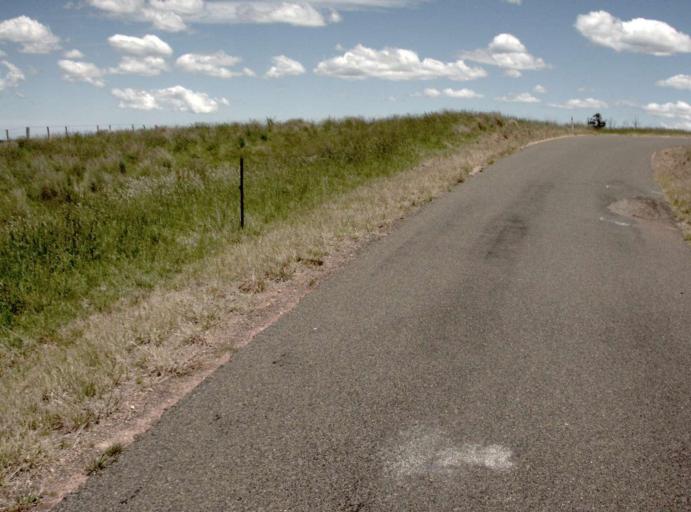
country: AU
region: New South Wales
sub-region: Snowy River
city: Jindabyne
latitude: -37.0933
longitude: 148.2658
